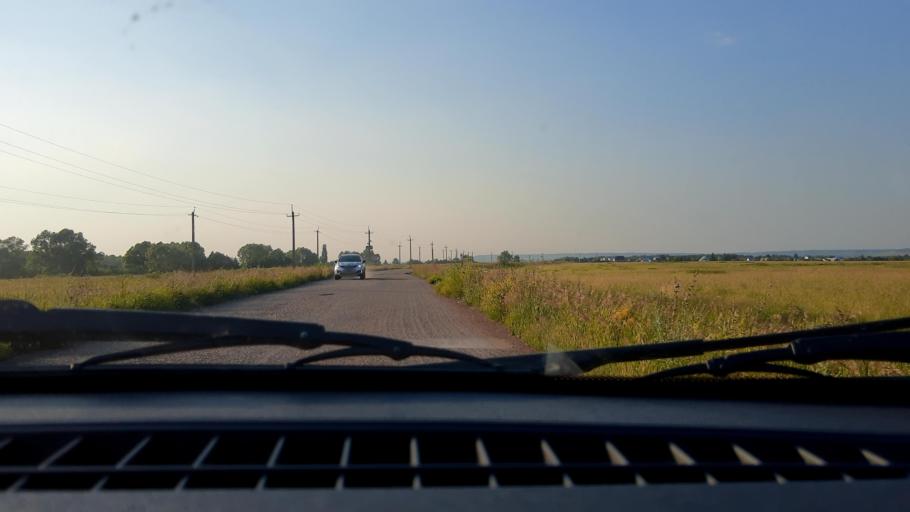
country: RU
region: Bashkortostan
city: Asanovo
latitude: 54.9075
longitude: 55.6268
